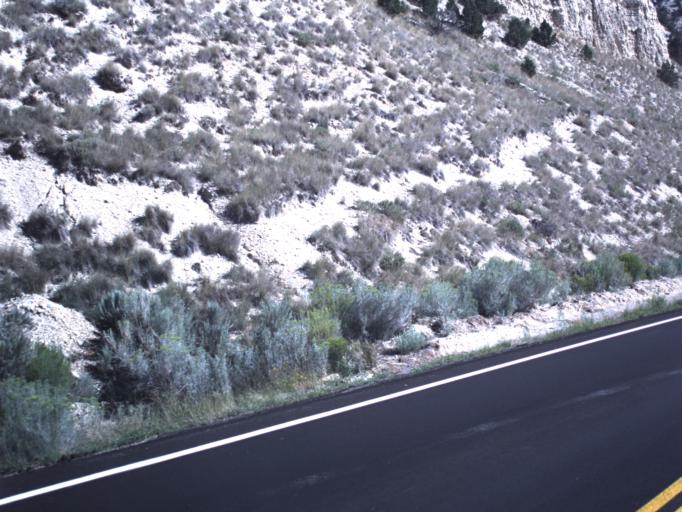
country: US
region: Utah
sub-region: Duchesne County
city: Duchesne
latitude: 40.0267
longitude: -110.5529
